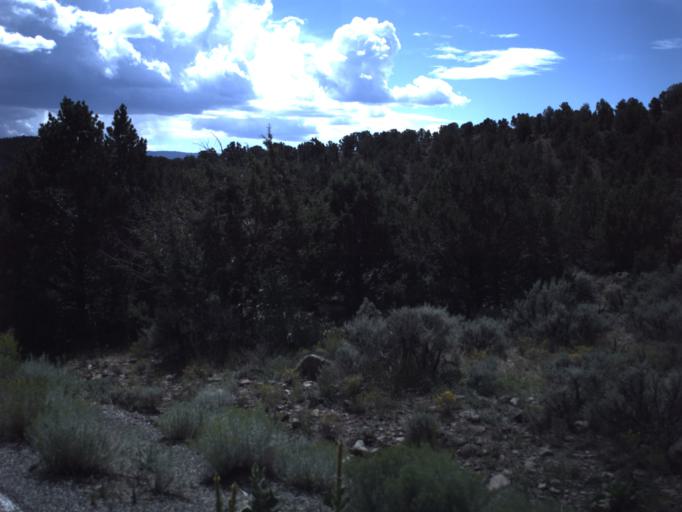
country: US
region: Utah
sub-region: Piute County
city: Junction
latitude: 38.2583
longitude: -112.2881
